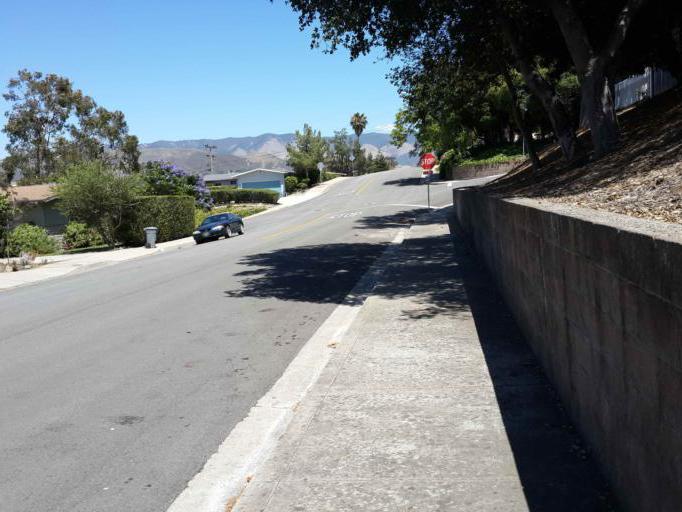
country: US
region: California
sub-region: San Luis Obispo County
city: San Luis Obispo
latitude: 35.2913
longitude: -120.6796
